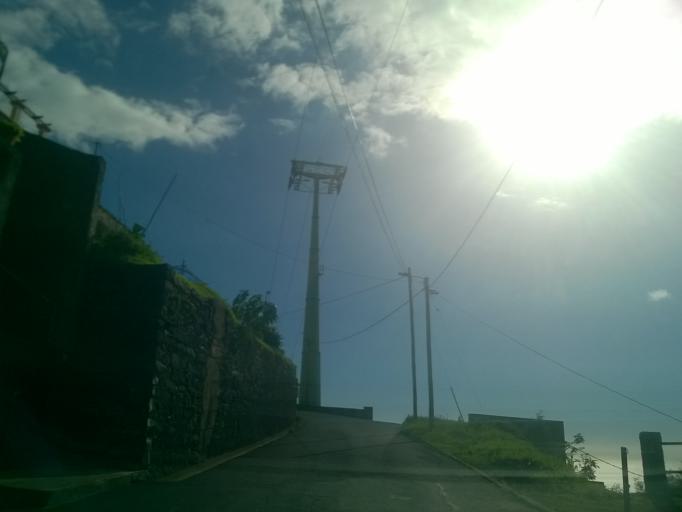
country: PT
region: Madeira
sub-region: Funchal
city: Nossa Senhora do Monte
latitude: 32.6713
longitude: -16.8989
